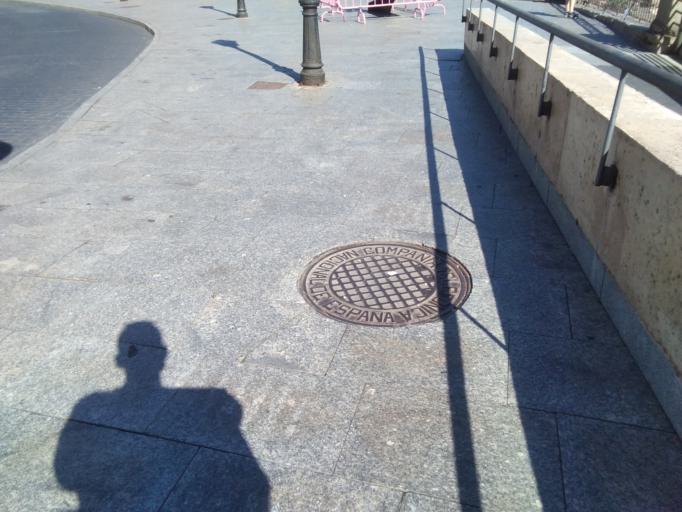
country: ES
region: Castille-La Mancha
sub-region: Province of Toledo
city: Toledo
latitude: 39.8613
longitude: -4.0217
